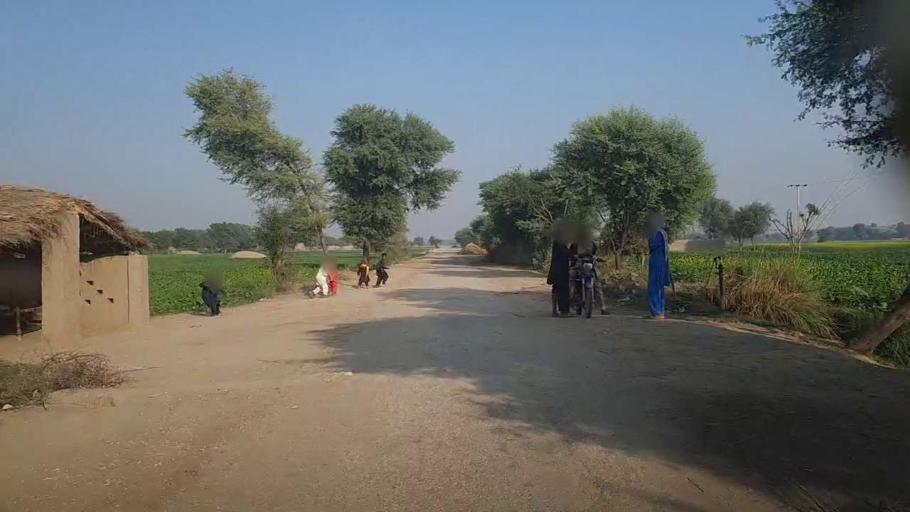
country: PK
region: Sindh
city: Kandiari
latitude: 26.7658
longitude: 68.4994
